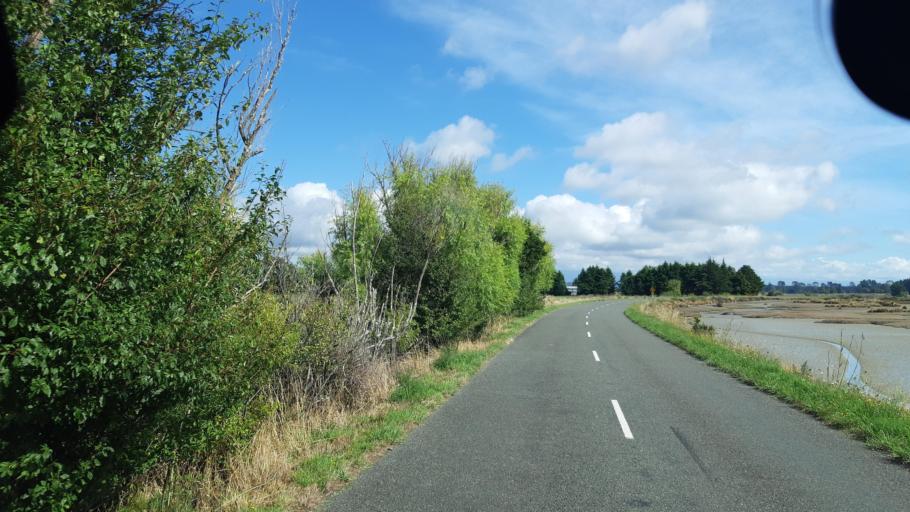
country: NZ
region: Tasman
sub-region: Tasman District
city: Richmond
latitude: -41.3011
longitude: 173.1516
